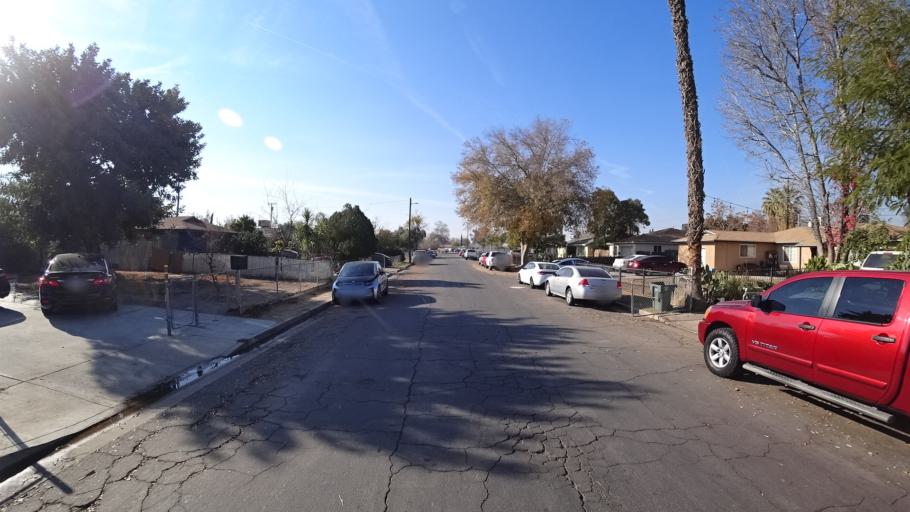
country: US
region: California
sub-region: Kern County
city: Bakersfield
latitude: 35.3266
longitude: -119.0133
